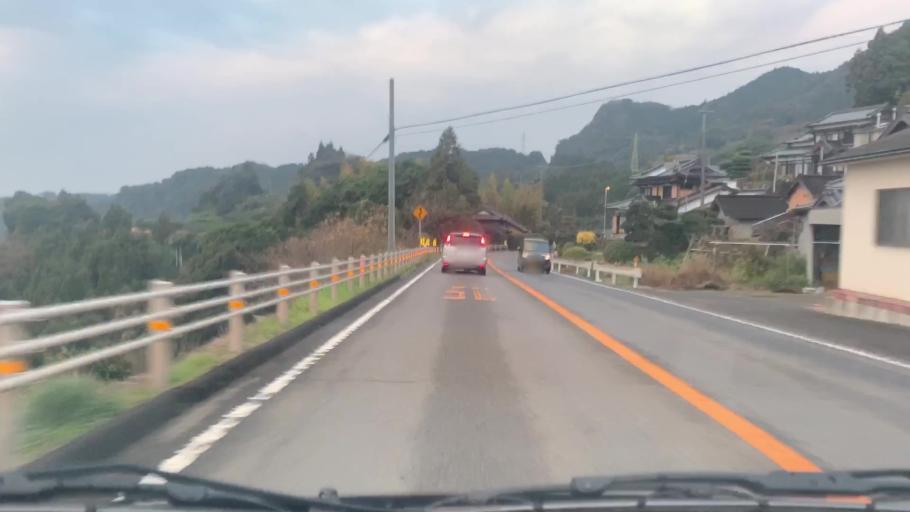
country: JP
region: Saga Prefecture
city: Ureshinomachi-shimojuku
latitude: 33.0594
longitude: 129.9517
